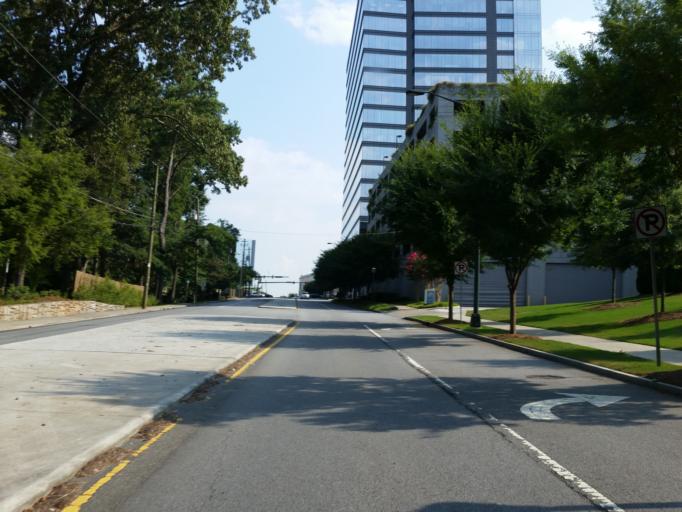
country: US
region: Georgia
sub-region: DeKalb County
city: North Atlanta
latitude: 33.8563
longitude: -84.3580
